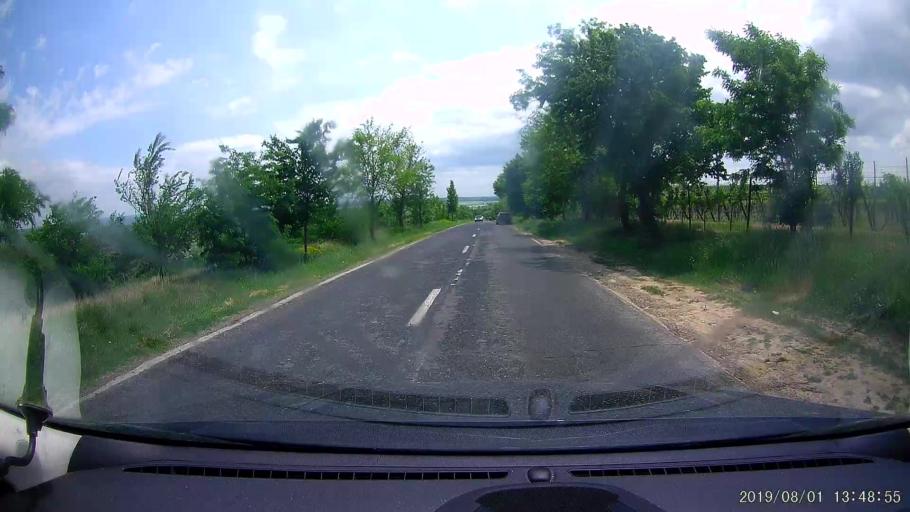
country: RO
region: Galati
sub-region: Comuna Oancea
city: Oancea
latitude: 45.9006
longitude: 28.1093
